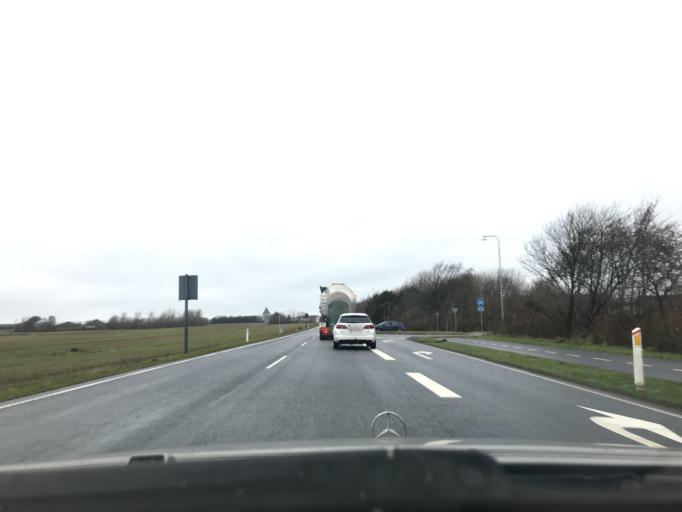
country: DK
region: South Denmark
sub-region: Tonder Kommune
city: Toftlund
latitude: 55.1862
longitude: 9.0581
